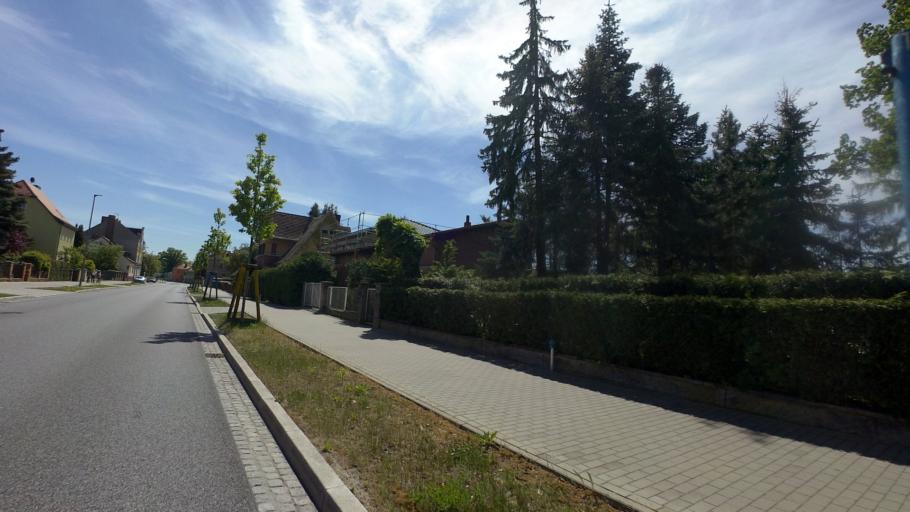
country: DE
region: Brandenburg
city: Luckenwalde
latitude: 52.0977
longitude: 13.1617
